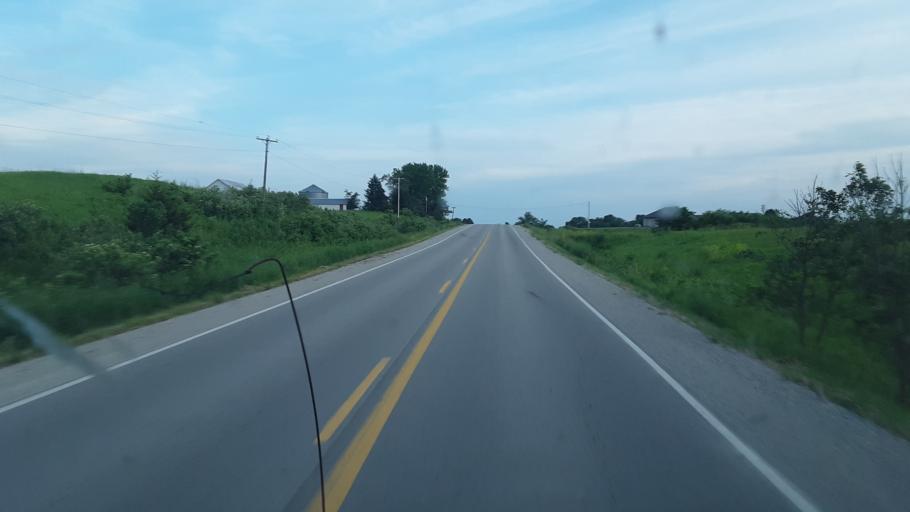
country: US
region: Iowa
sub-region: Iowa County
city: Marengo
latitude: 41.7267
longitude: -92.1826
